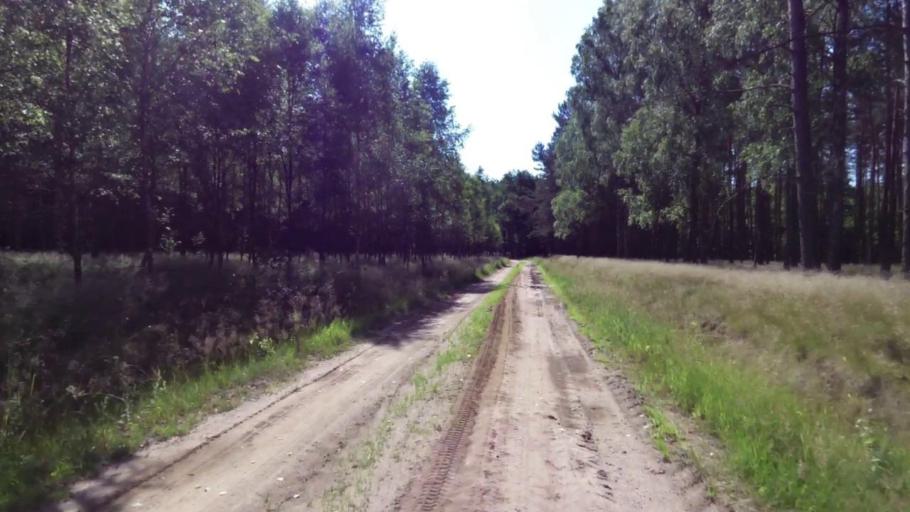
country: PL
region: West Pomeranian Voivodeship
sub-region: Powiat swidwinski
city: Polczyn-Zdroj
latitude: 53.8696
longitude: 16.1187
